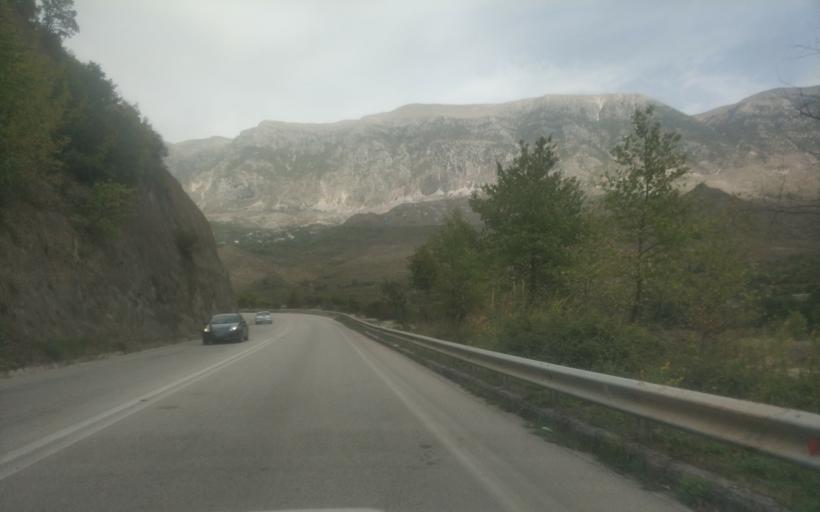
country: AL
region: Gjirokaster
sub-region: Rrethi i Gjirokastres
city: Picar
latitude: 40.2202
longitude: 20.0863
